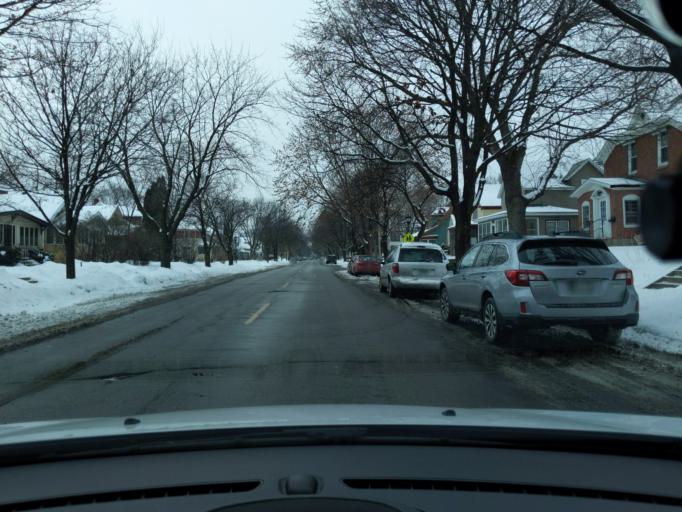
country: US
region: Minnesota
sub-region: Ramsey County
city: Falcon Heights
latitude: 44.9594
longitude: -93.1531
